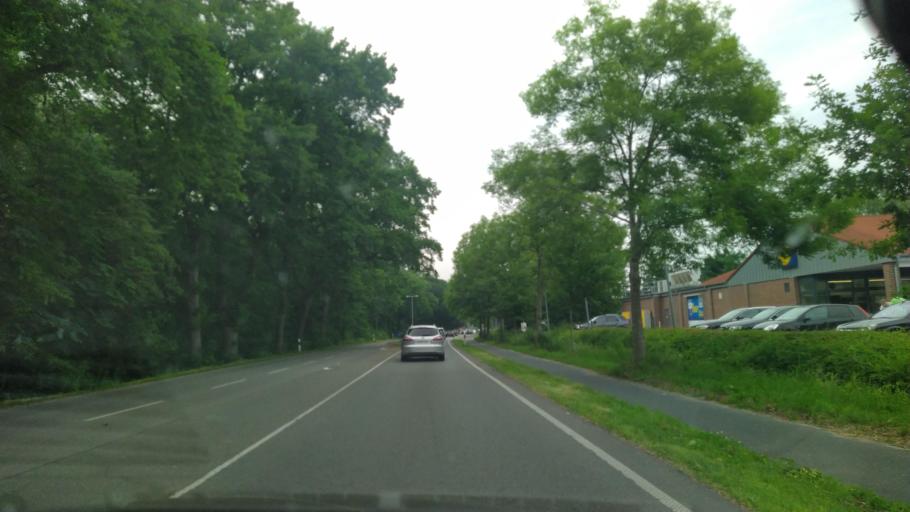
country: DE
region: Lower Saxony
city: Leer
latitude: 53.2314
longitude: 7.4770
